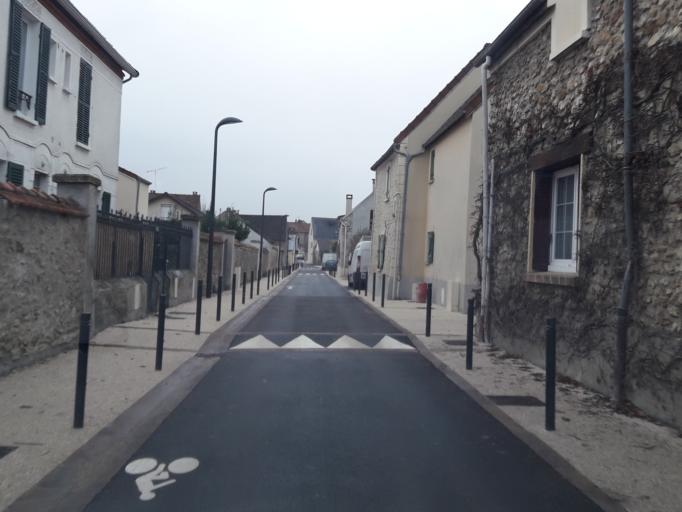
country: FR
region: Ile-de-France
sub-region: Departement de l'Essonne
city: Vert-le-Petit
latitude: 48.5532
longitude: 2.3690
